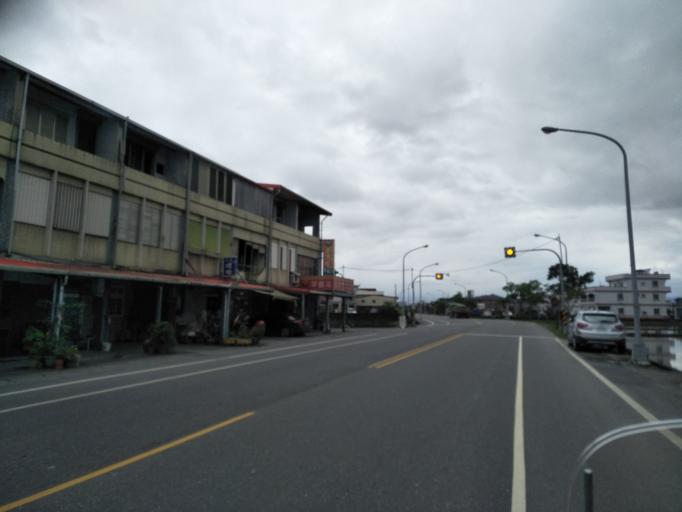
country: TW
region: Taiwan
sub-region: Yilan
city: Yilan
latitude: 24.7933
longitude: 121.7848
